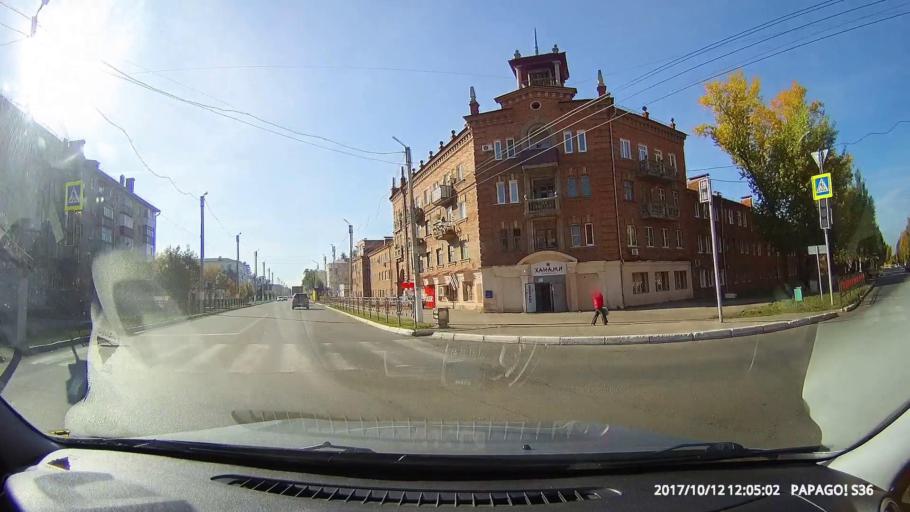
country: RU
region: Samara
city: Chapayevsk
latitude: 52.9790
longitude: 49.7137
